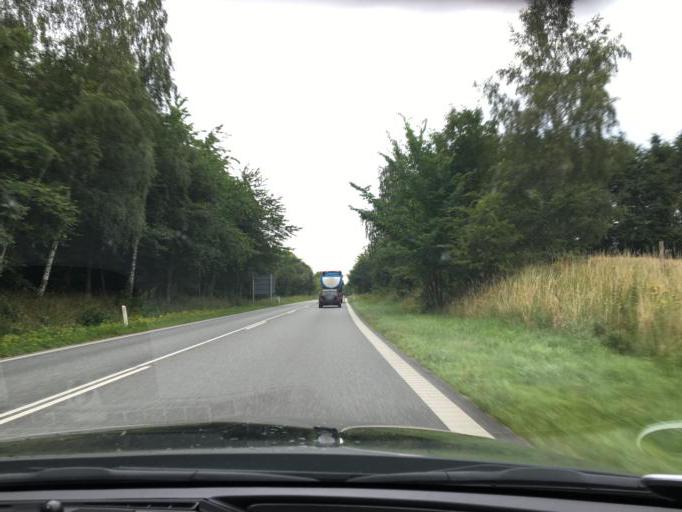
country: DK
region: Capital Region
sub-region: Hillerod Kommune
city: Nodebo
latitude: 55.9385
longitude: 12.3559
